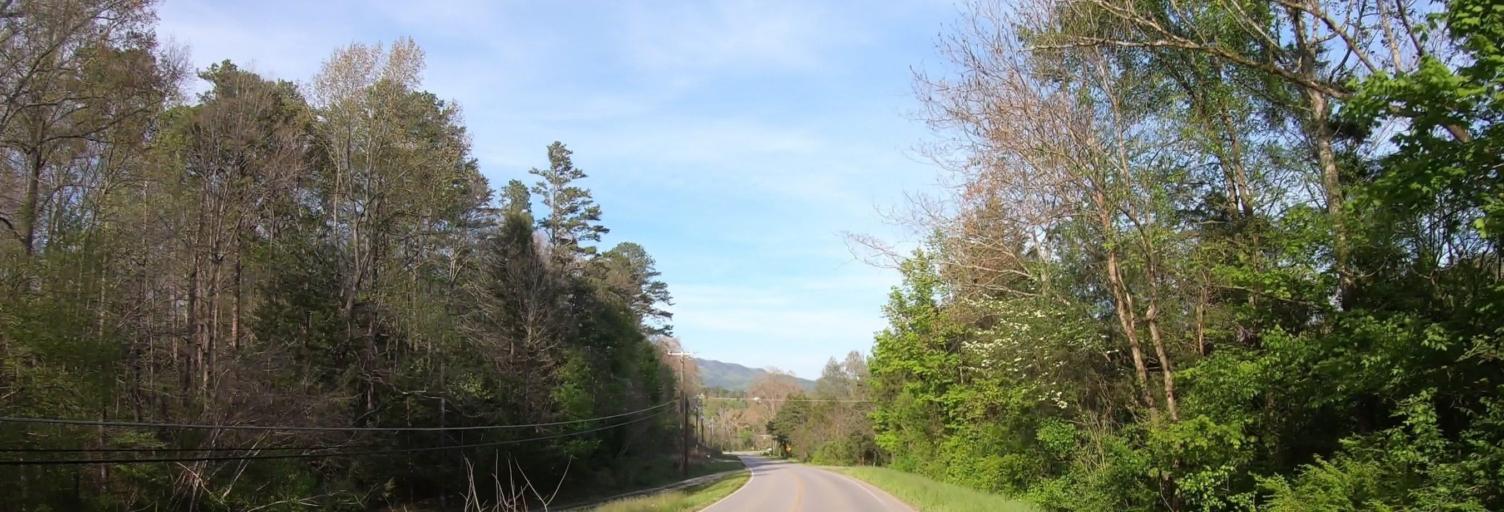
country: US
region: Tennessee
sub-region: Blount County
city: Wildwood
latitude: 35.6739
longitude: -83.7694
